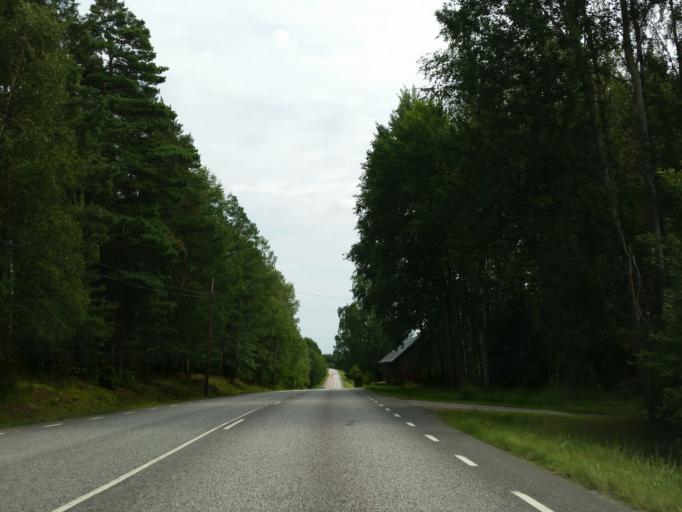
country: SE
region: Soedermanland
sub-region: Strangnas Kommun
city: Mariefred
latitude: 59.2247
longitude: 17.2212
